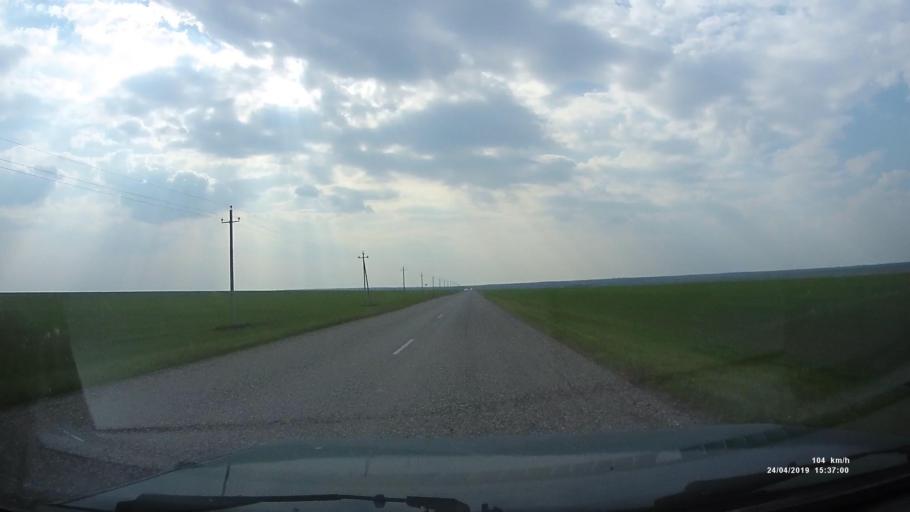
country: RU
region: Kalmykiya
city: Yashalta
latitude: 46.5993
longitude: 42.8588
